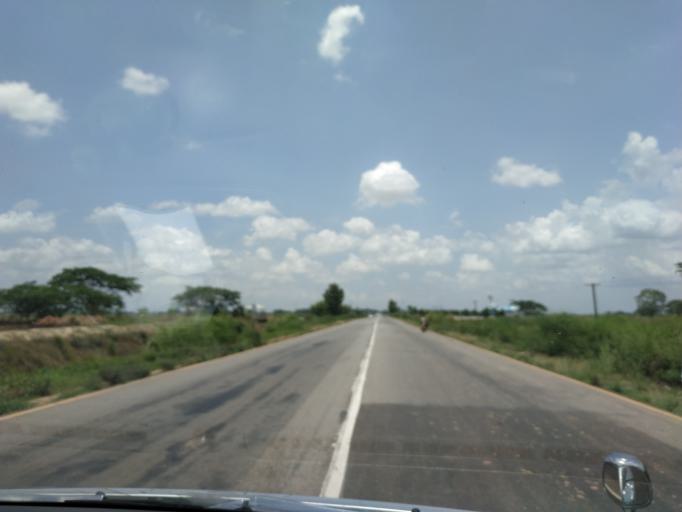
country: MM
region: Bago
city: Thanatpin
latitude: 17.4562
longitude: 96.6073
